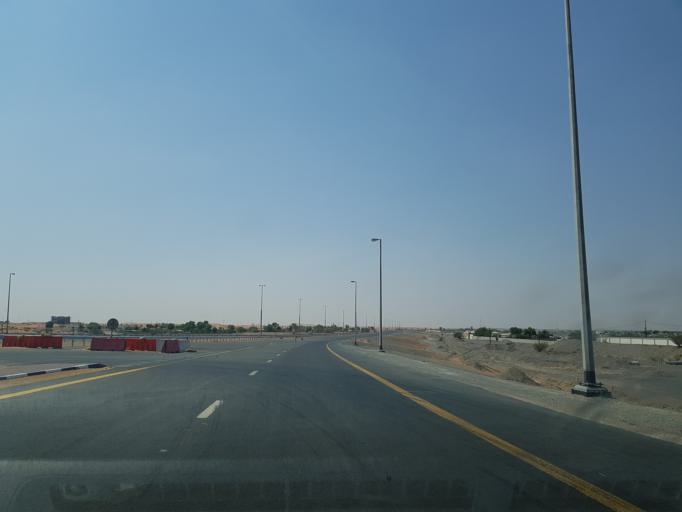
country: AE
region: Ash Shariqah
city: Adh Dhayd
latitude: 25.2324
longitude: 55.9136
